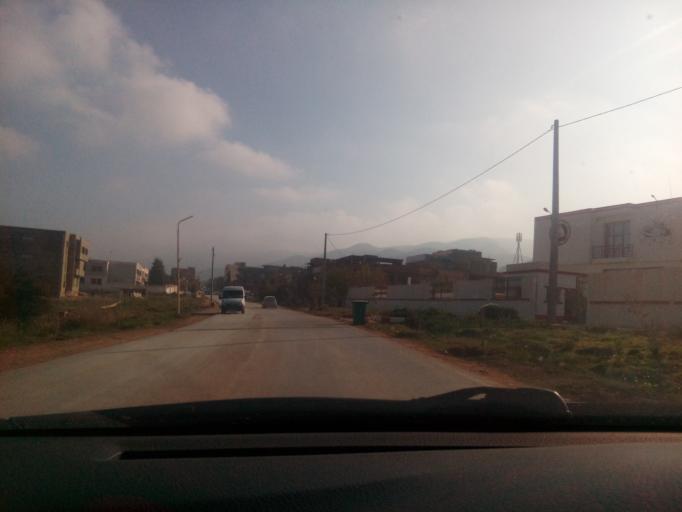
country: DZ
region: Oran
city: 'Ain el Turk
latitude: 35.7028
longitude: -0.8213
